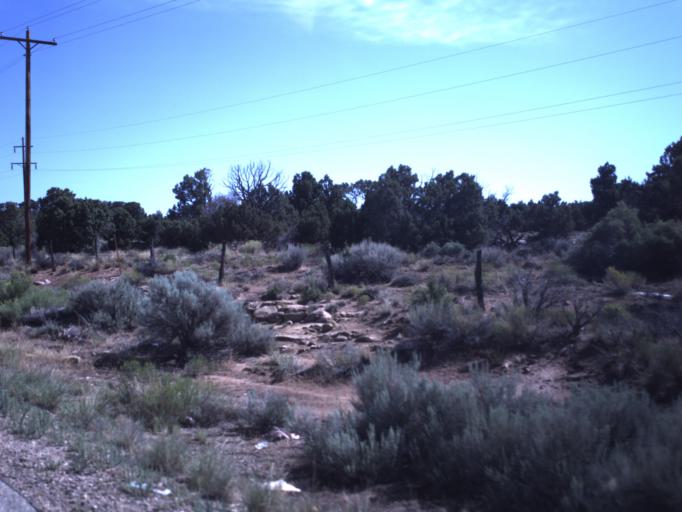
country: US
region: Utah
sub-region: Duchesne County
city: Duchesne
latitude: 40.2882
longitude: -110.3764
